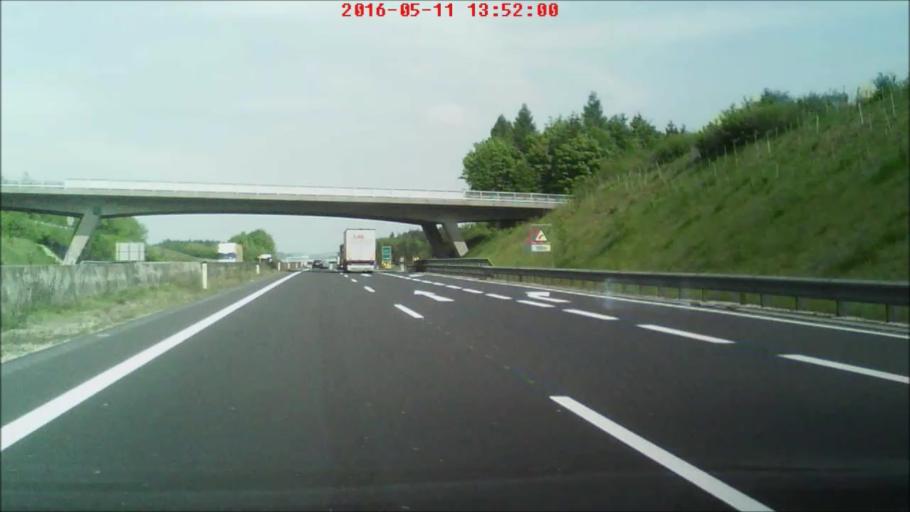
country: AT
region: Upper Austria
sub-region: Politischer Bezirk Vocklabruck
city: Niederthalheim
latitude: 48.1790
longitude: 13.7442
